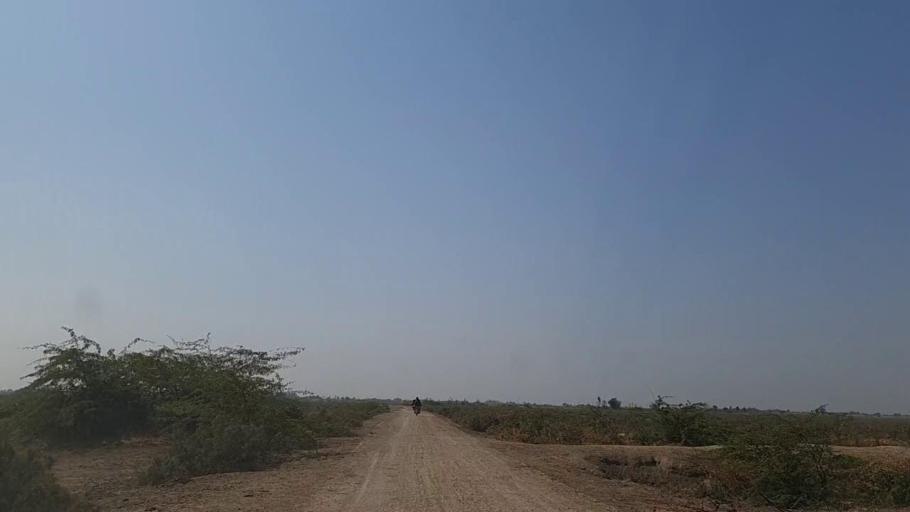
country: PK
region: Sindh
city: Digri
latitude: 24.9695
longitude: 69.2052
